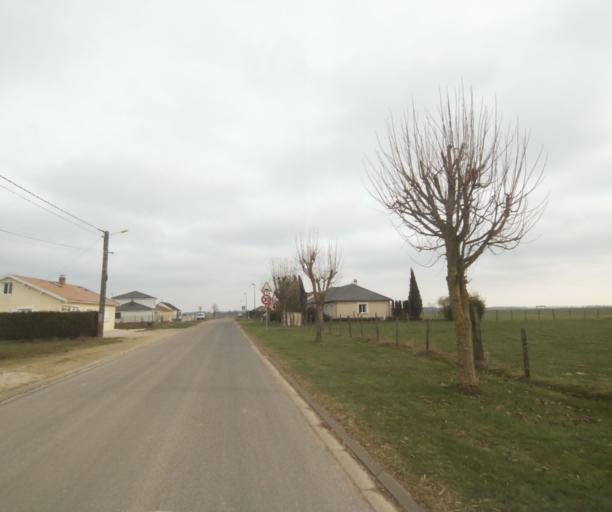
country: FR
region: Champagne-Ardenne
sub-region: Departement de la Haute-Marne
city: Villiers-en-Lieu
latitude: 48.6832
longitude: 4.8377
